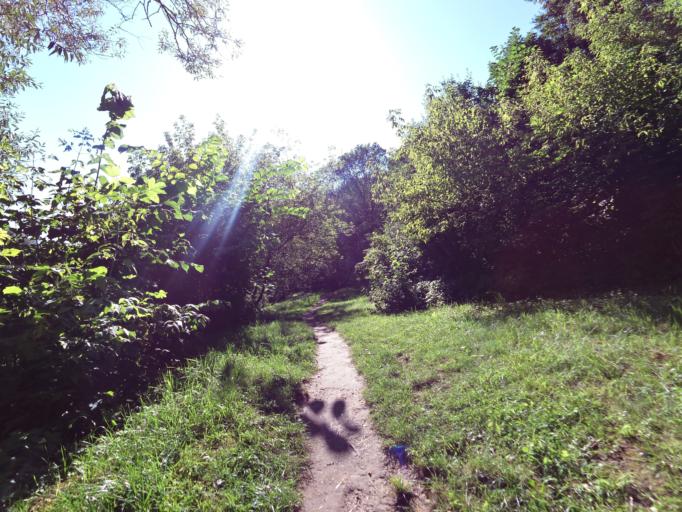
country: LT
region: Vilnius County
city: Vilkpede
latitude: 54.6893
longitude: 25.2302
